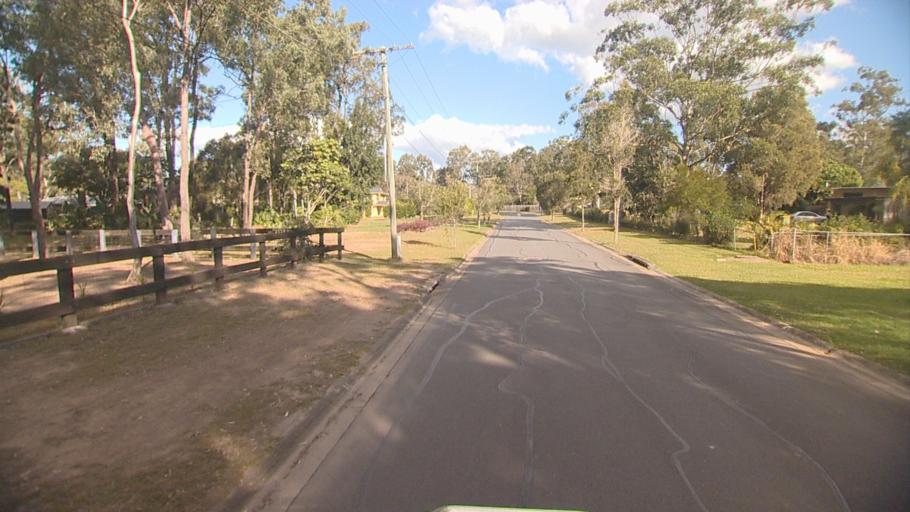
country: AU
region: Queensland
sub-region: Logan
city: Beenleigh
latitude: -27.6699
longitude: 153.2079
